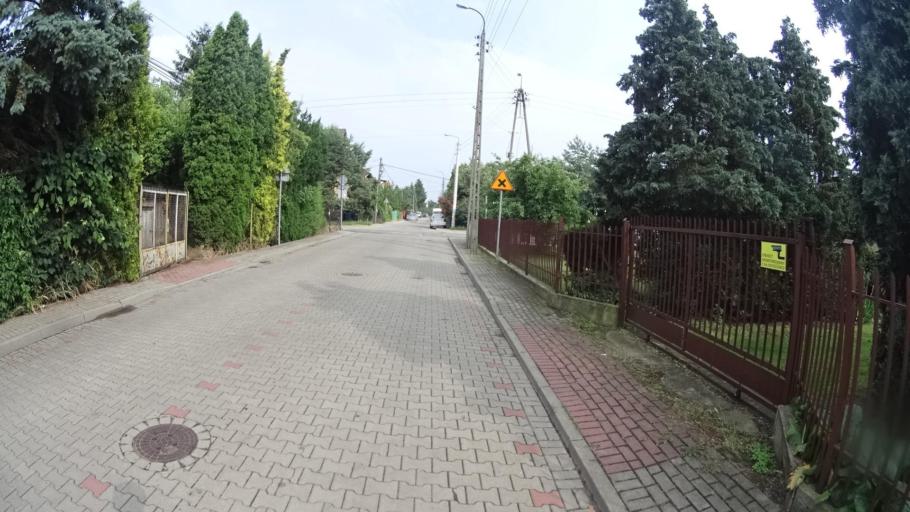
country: PL
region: Masovian Voivodeship
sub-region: Powiat pruszkowski
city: Raszyn
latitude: 52.1621
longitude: 20.9240
